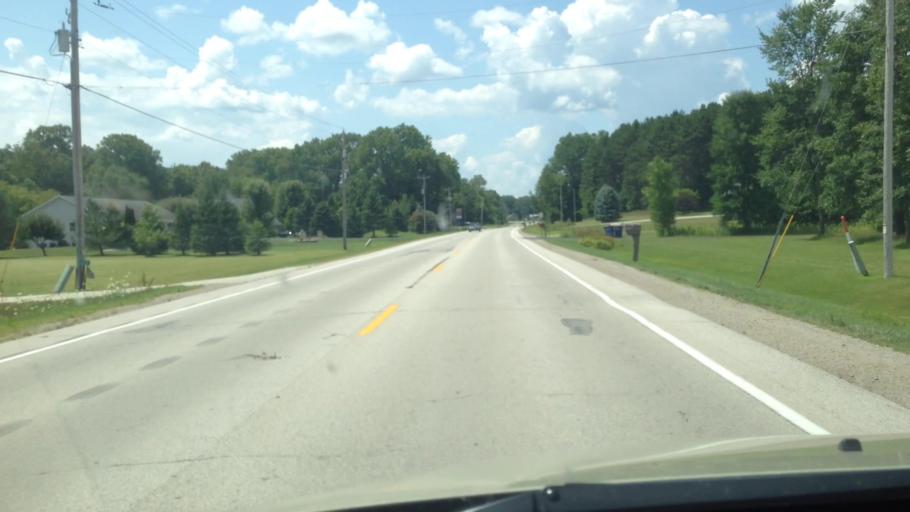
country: US
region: Wisconsin
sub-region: Brown County
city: Suamico
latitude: 44.6465
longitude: -88.1021
